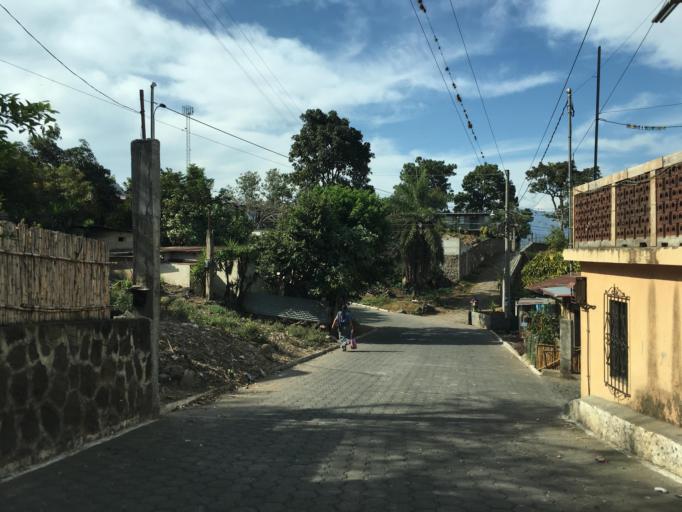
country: GT
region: Solola
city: San Antonio Palopo
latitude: 14.6594
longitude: -91.1585
